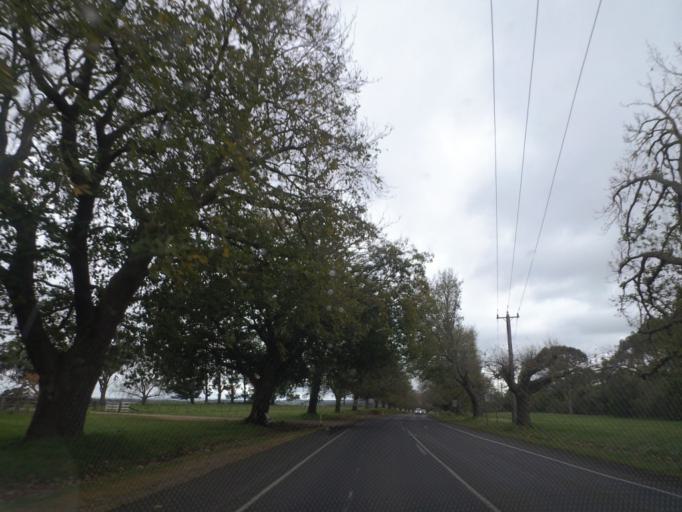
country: AU
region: Victoria
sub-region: Hume
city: Sunbury
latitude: -37.3419
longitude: 144.5296
